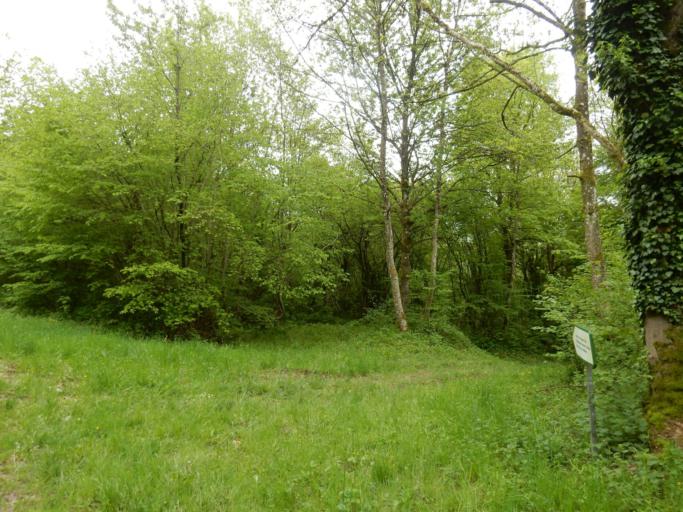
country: FR
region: Lorraine
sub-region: Departement de la Meuse
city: Verdun
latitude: 49.2144
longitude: 5.4476
